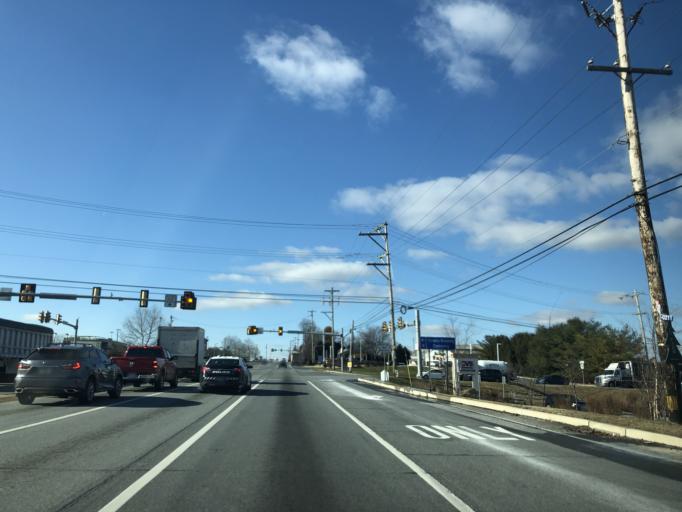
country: US
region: Pennsylvania
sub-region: Chester County
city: Parkesburg
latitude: 39.9834
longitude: -75.9306
